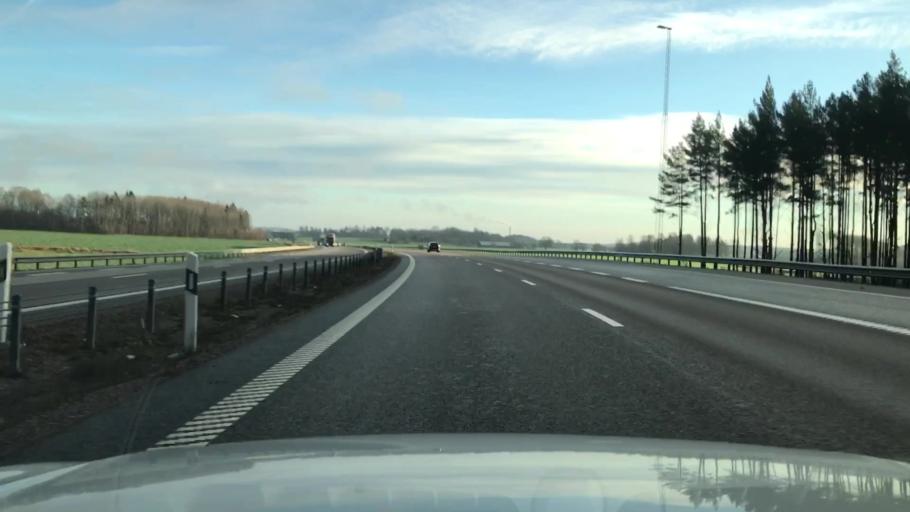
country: SE
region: Soedermanland
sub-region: Nykopings Kommun
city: Nykoping
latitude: 58.7460
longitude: 16.9429
